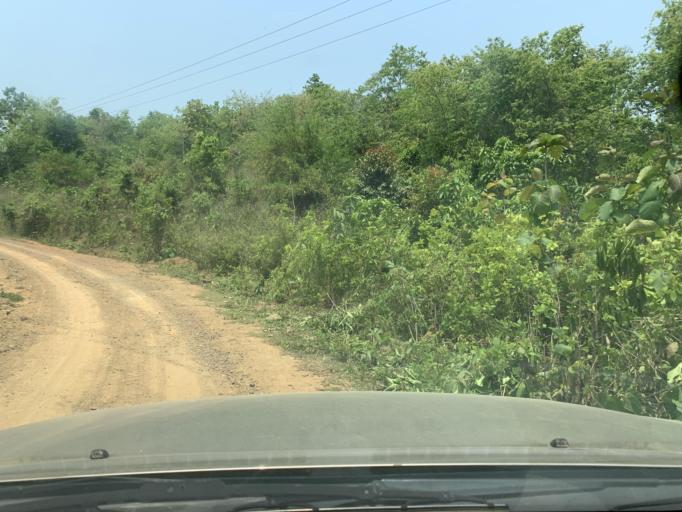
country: LA
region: Louangphabang
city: Louangphabang
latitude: 19.9504
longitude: 102.1316
